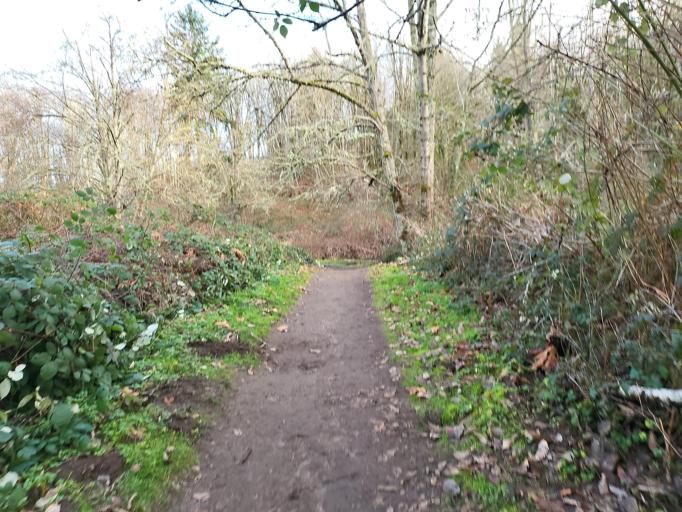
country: US
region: Washington
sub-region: King County
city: Newcastle
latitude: 47.5423
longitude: -122.1523
